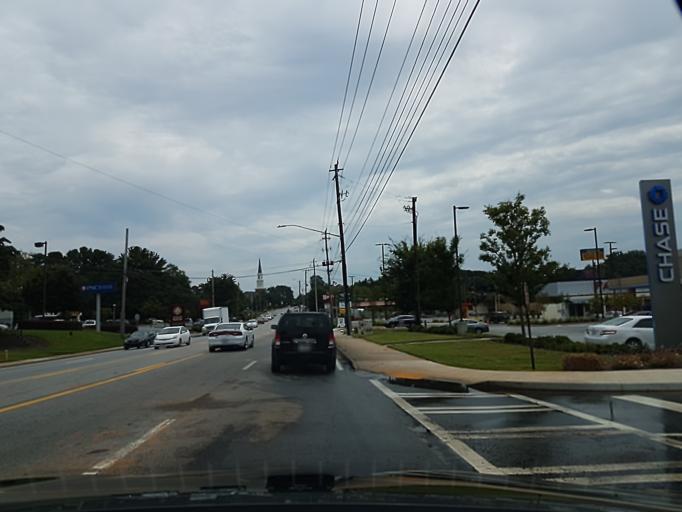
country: US
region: Georgia
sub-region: DeKalb County
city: North Druid Hills
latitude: 33.8165
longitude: -84.3111
